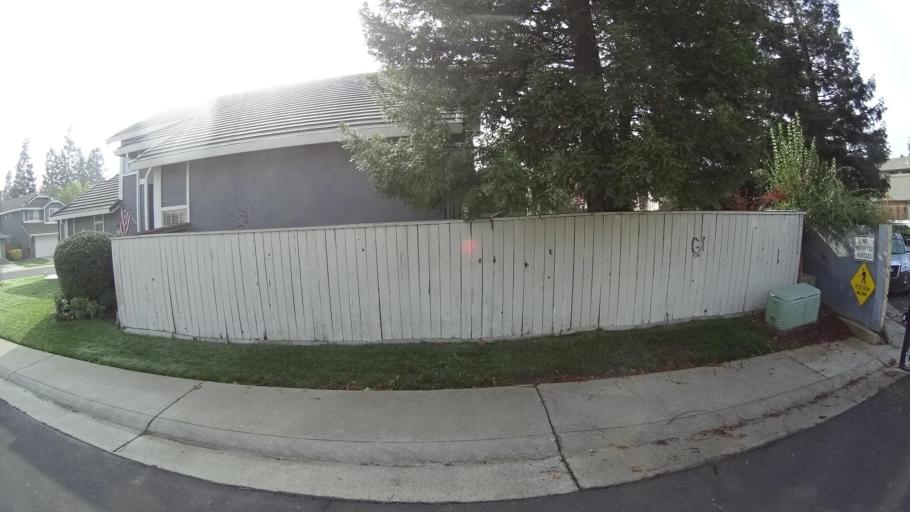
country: US
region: California
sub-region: Sacramento County
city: Elk Grove
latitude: 38.3904
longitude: -121.3669
